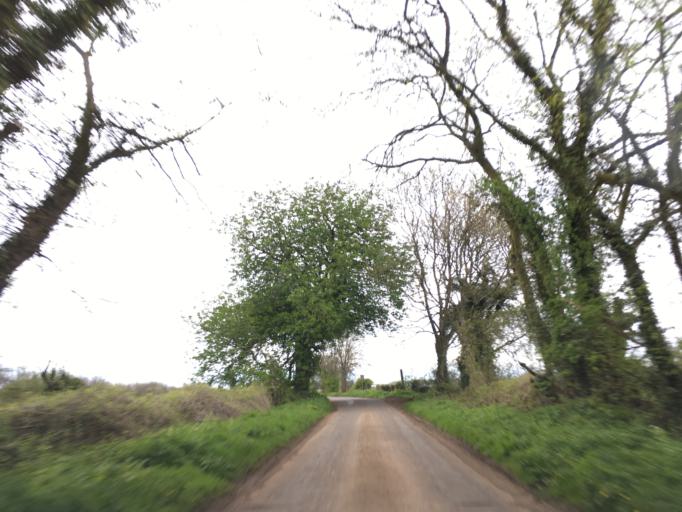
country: GB
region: England
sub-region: Gloucestershire
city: Wotton-under-Edge
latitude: 51.6529
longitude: -2.3017
